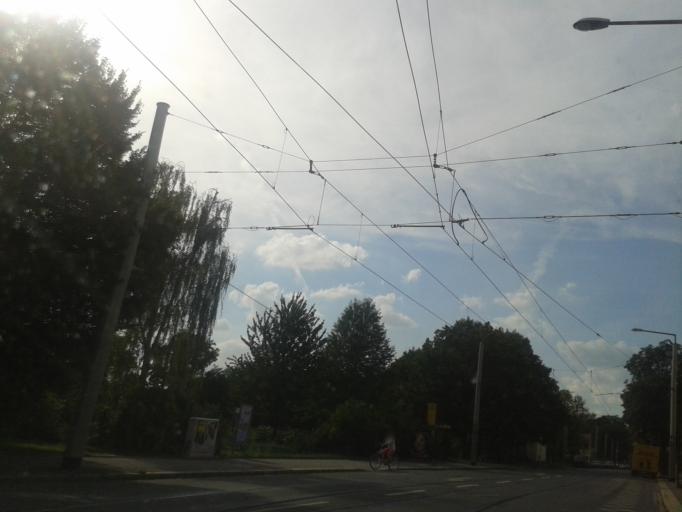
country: DE
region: Saxony
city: Dresden
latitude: 51.0223
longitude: 13.7657
